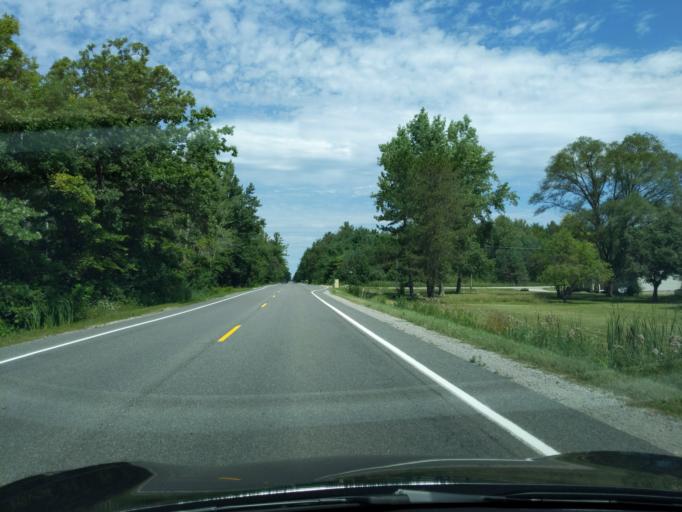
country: US
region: Michigan
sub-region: Midland County
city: Midland
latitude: 43.5823
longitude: -84.3694
